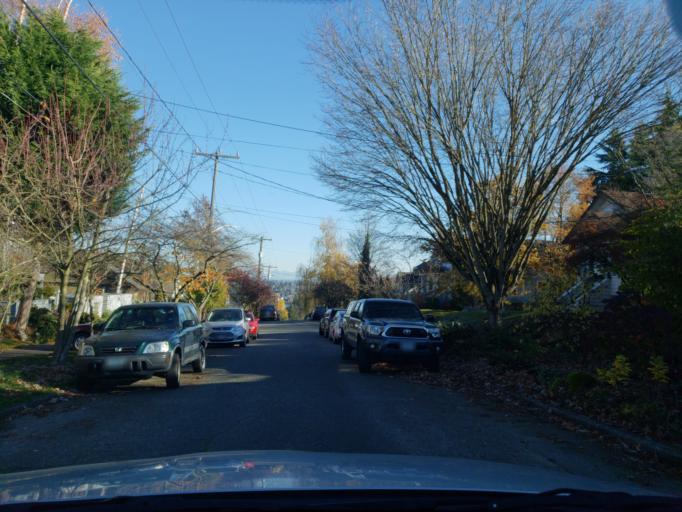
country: US
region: Washington
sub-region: King County
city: Seattle
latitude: 47.6739
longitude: -122.3535
